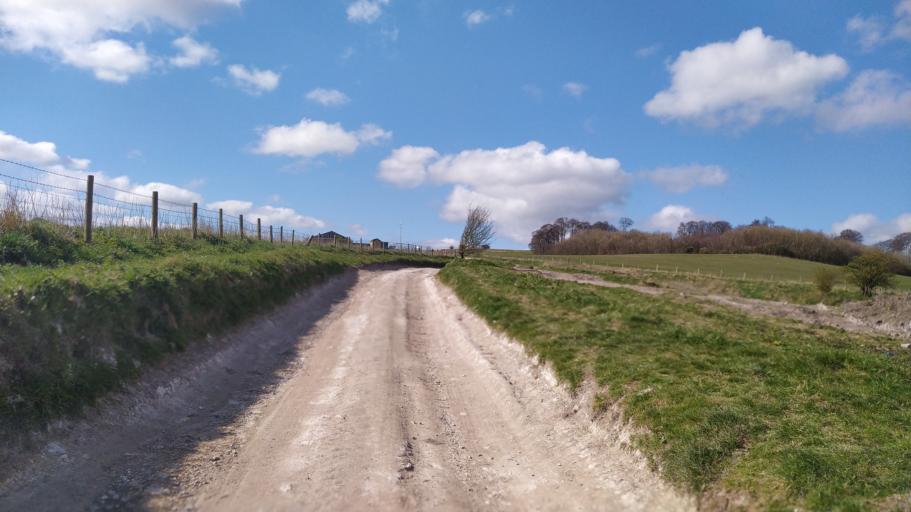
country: GB
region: England
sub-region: Wiltshire
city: Avebury
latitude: 51.4279
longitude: -1.9223
